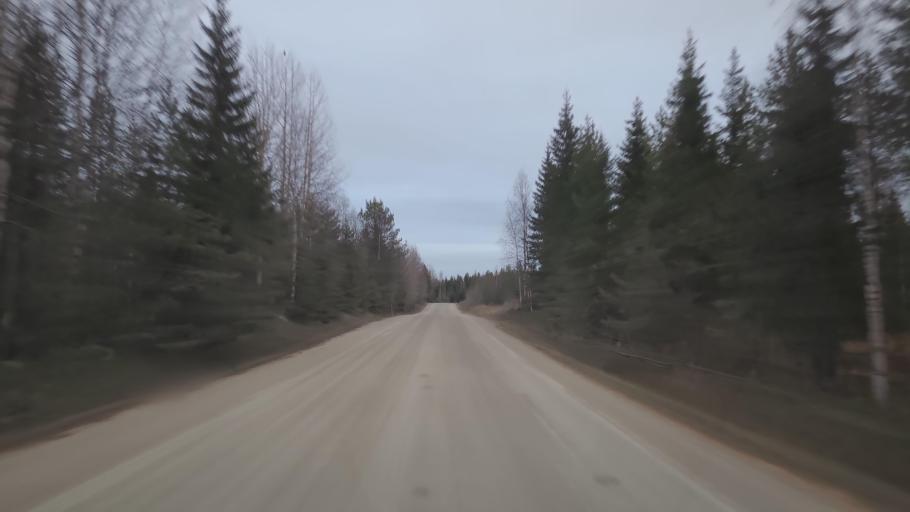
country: FI
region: Lapland
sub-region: Kemi-Tornio
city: Tervola
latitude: 66.0711
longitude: 24.8802
